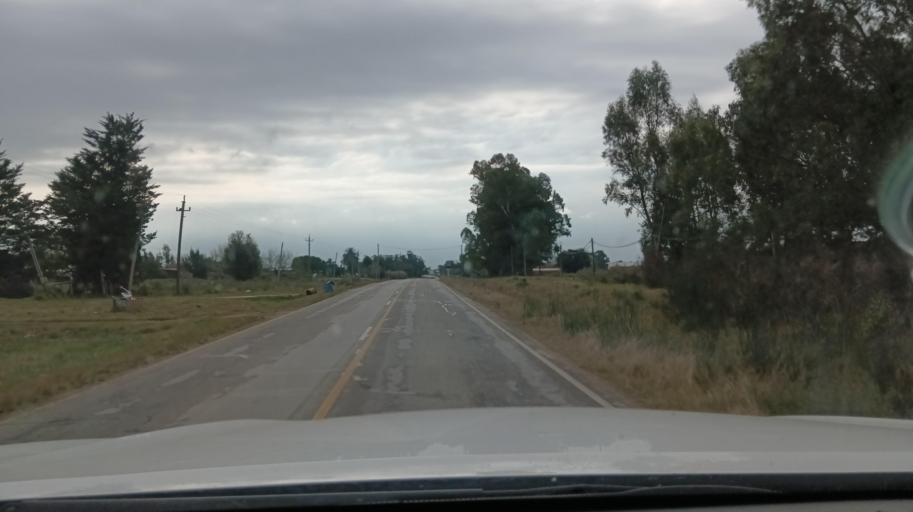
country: UY
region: Canelones
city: Sauce
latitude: -34.6341
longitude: -56.1091
